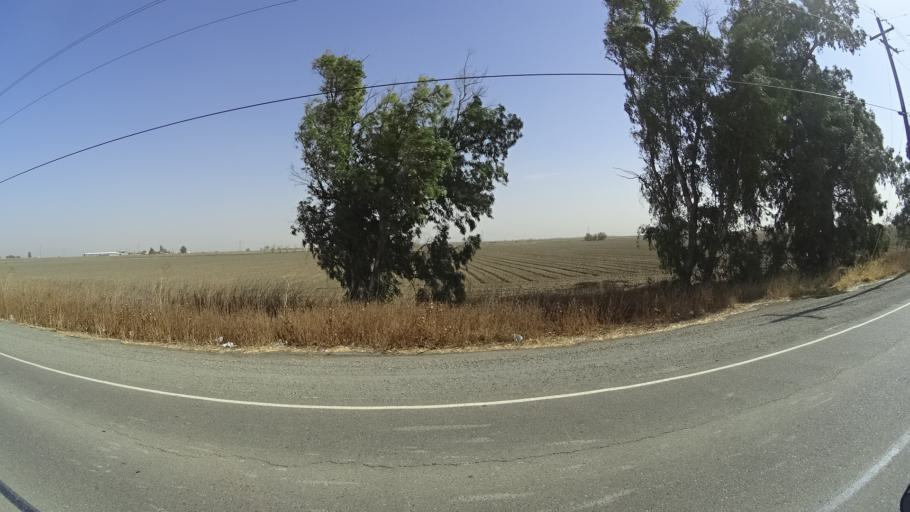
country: US
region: California
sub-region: Yolo County
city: Davis
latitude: 38.5864
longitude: -121.6749
